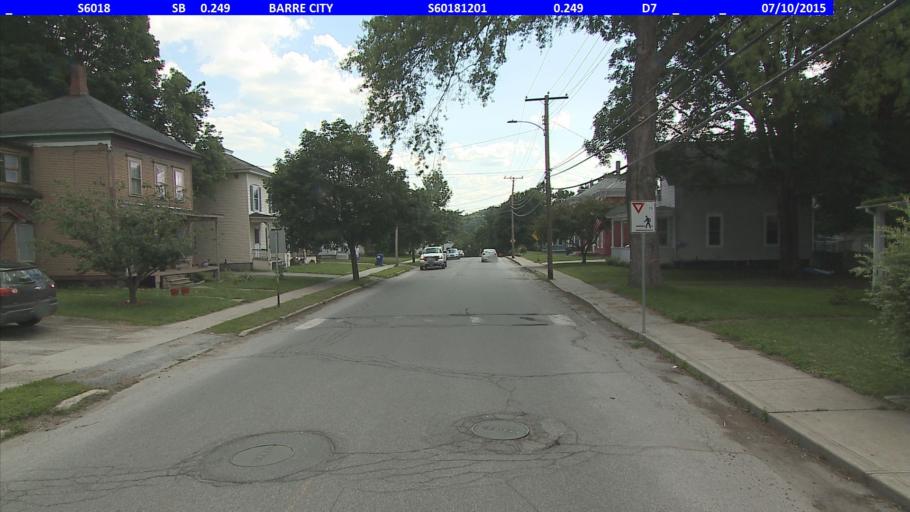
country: US
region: Vermont
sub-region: Washington County
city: Barre
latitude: 44.2025
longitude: -72.5018
